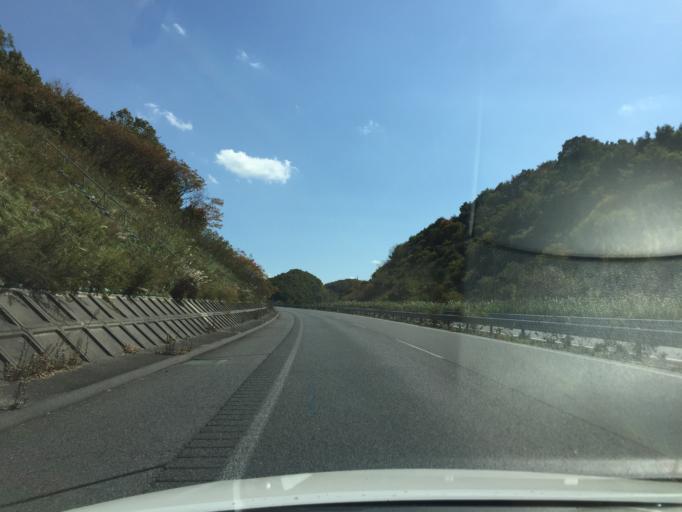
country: JP
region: Fukushima
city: Funehikimachi-funehiki
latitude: 37.2337
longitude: 140.6792
